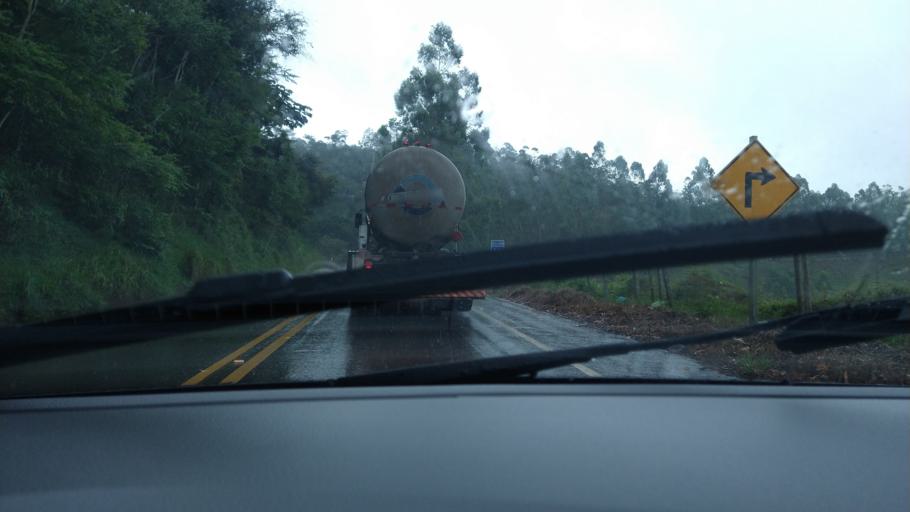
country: BR
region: Minas Gerais
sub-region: Ponte Nova
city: Ponte Nova
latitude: -20.5812
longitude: -42.8794
